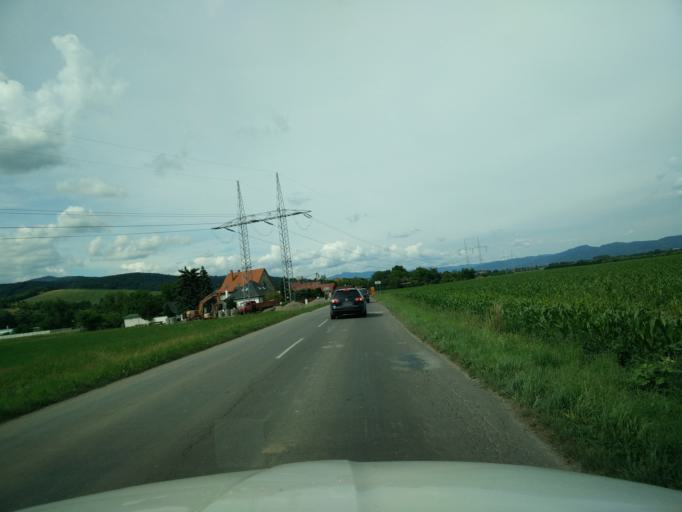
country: SK
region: Nitriansky
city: Bojnice
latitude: 48.7561
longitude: 18.5719
